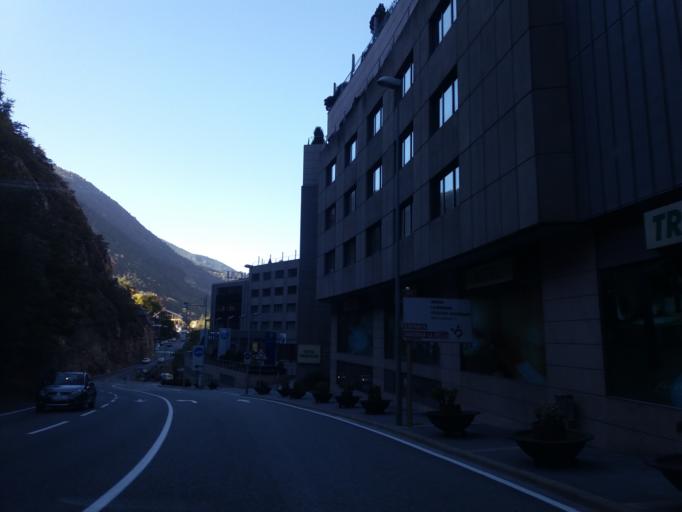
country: AD
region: Escaldes-Engordany
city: les Escaldes
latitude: 42.5131
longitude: 1.5516
